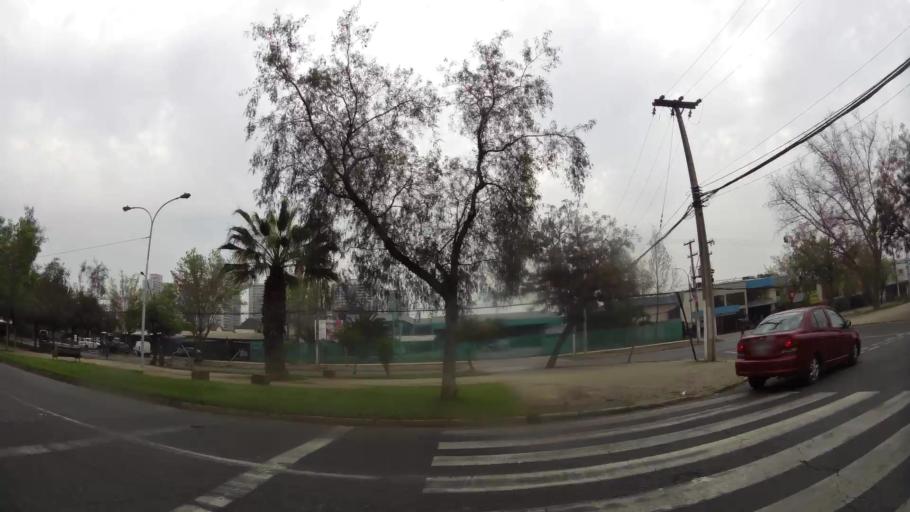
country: CL
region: Santiago Metropolitan
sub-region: Provincia de Santiago
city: Villa Presidente Frei, Nunoa, Santiago, Chile
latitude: -33.4879
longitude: -70.6119
